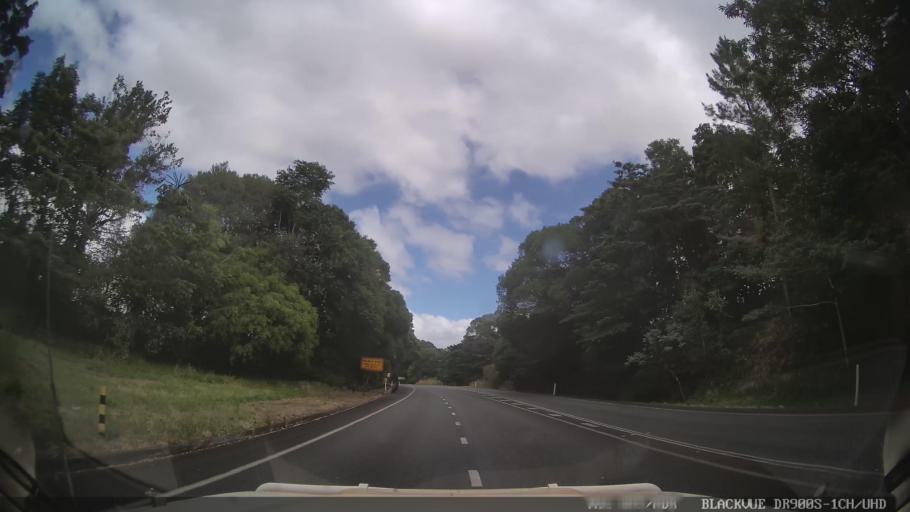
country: AU
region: Queensland
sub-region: Tablelands
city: Tolga
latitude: -17.2215
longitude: 145.6666
